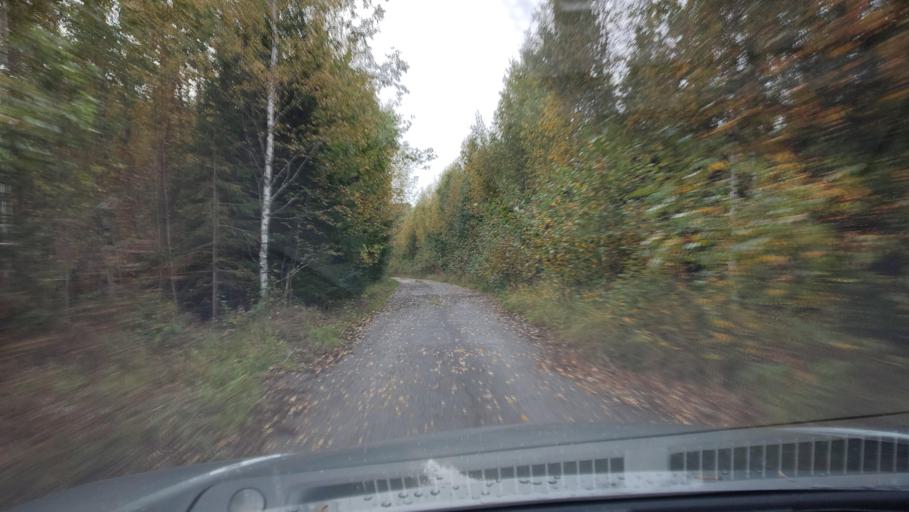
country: FI
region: Ostrobothnia
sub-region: Sydosterbotten
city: Kristinestad
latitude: 62.2684
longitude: 21.4570
